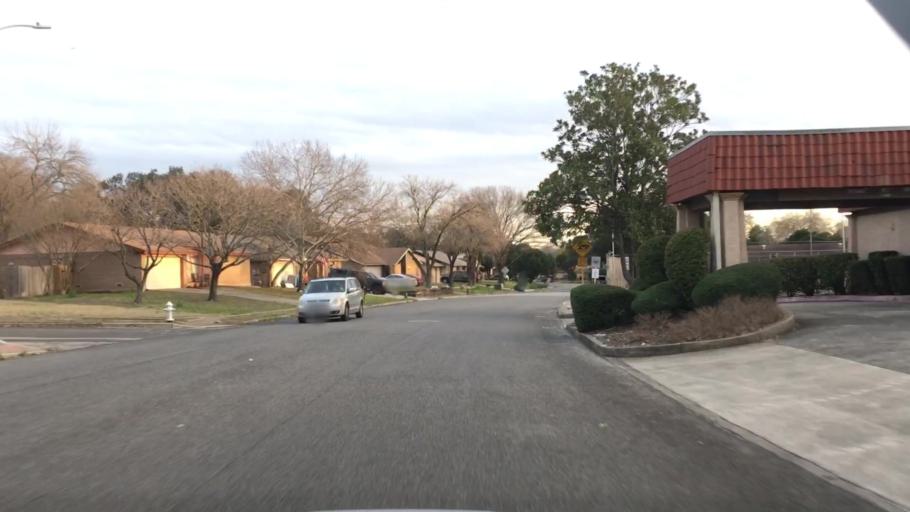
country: US
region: Texas
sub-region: Bexar County
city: Windcrest
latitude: 29.5593
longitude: -98.3938
